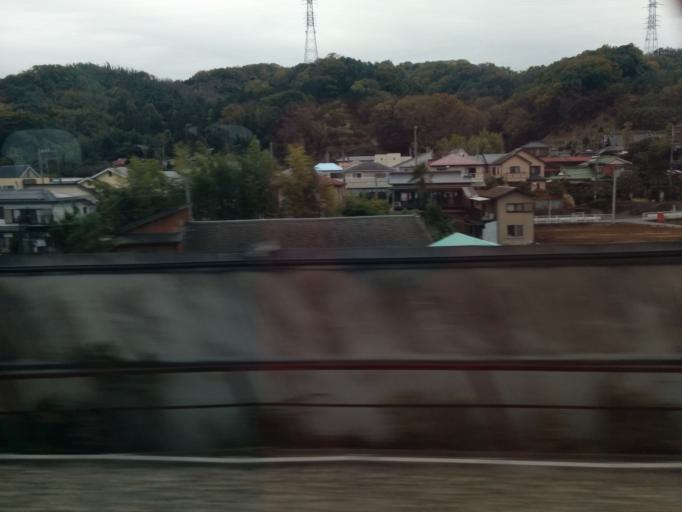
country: JP
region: Kanagawa
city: Oiso
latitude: 35.3252
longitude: 139.2896
